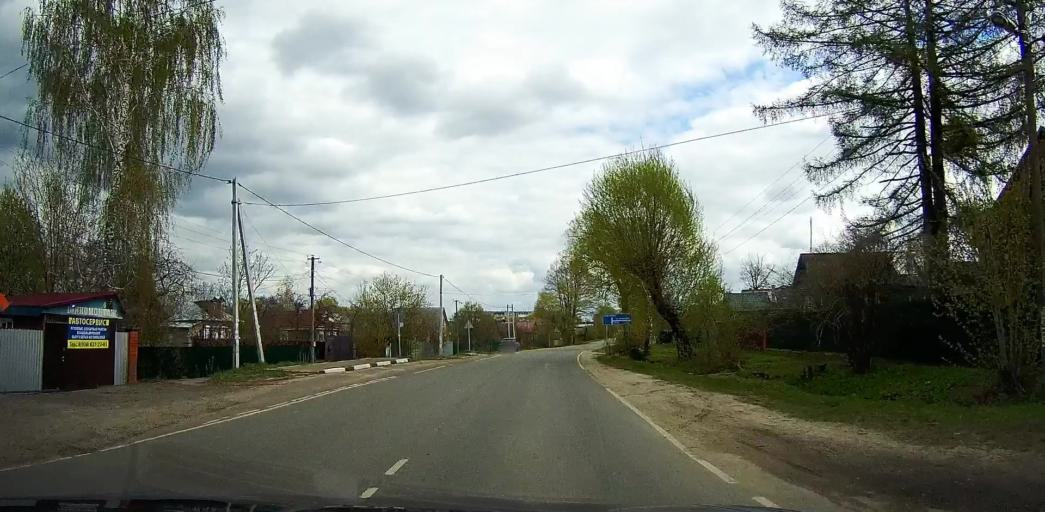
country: RU
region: Moskovskaya
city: Imeni Tsyurupy
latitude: 55.4971
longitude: 38.6400
